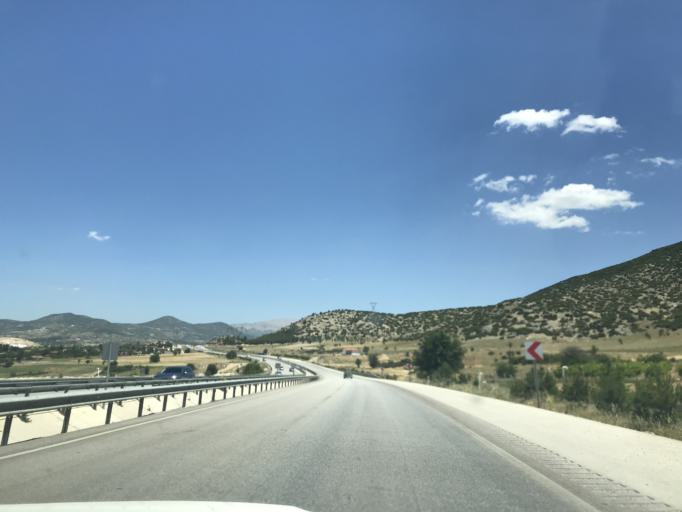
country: TR
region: Isparta
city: Gonen
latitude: 37.8454
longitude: 30.4215
